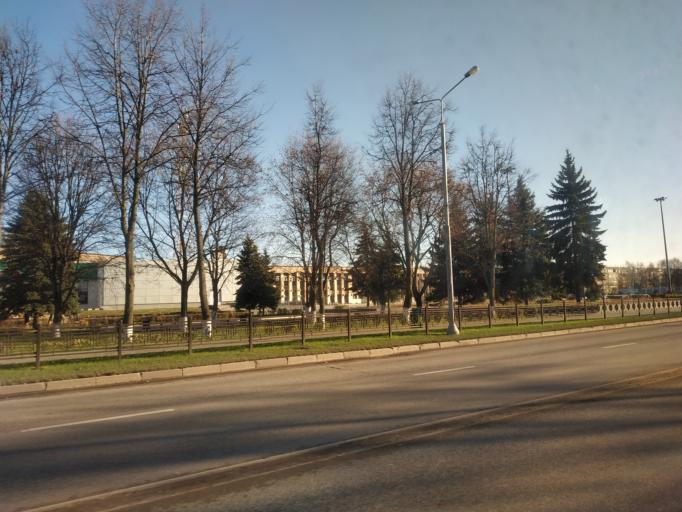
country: RU
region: Moskovskaya
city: Domodedovo
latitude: 55.4380
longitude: 37.7665
